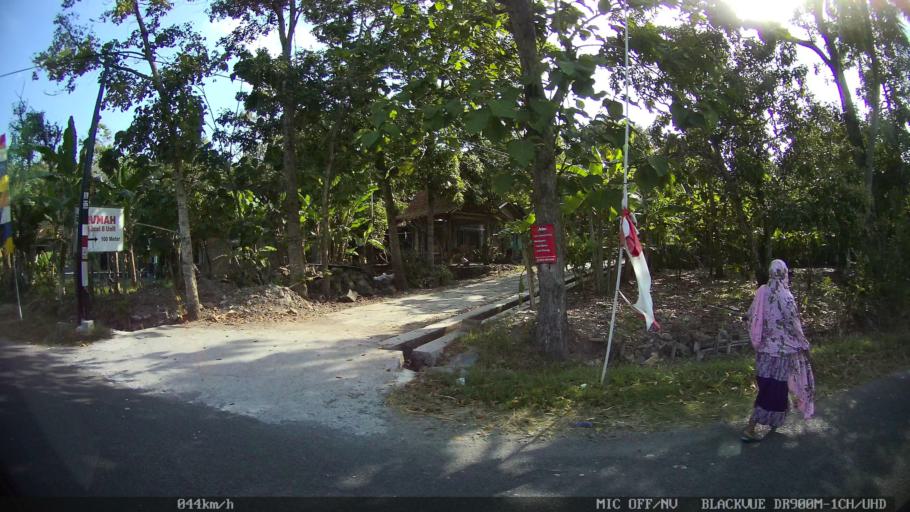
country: ID
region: Daerah Istimewa Yogyakarta
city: Kasihan
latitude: -7.8527
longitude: 110.3185
